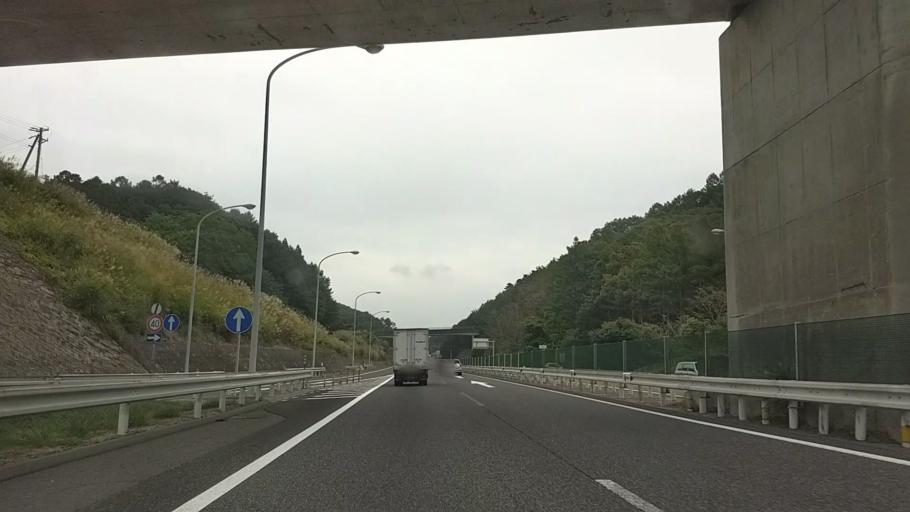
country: JP
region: Nagano
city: Shiojiri
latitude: 36.1172
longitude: 137.9825
